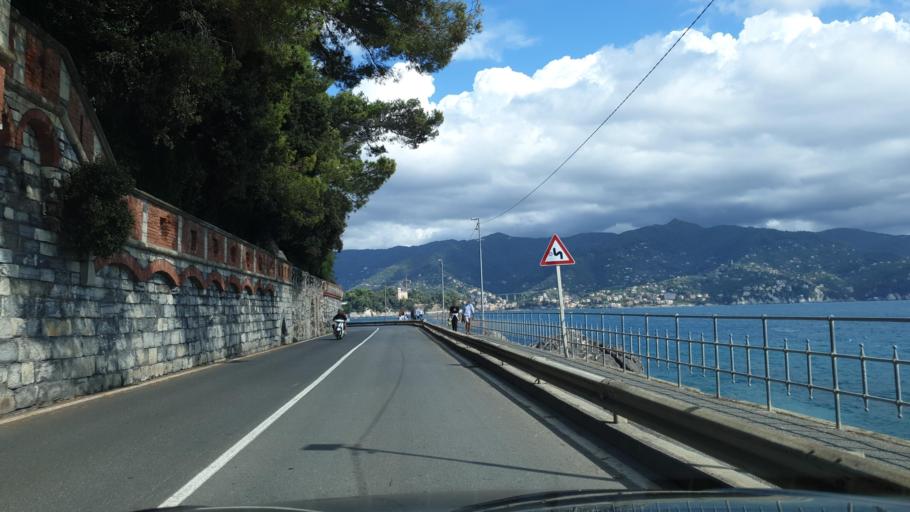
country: IT
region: Liguria
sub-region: Provincia di Genova
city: Santa Margherita Ligure
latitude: 44.3234
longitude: 9.2160
